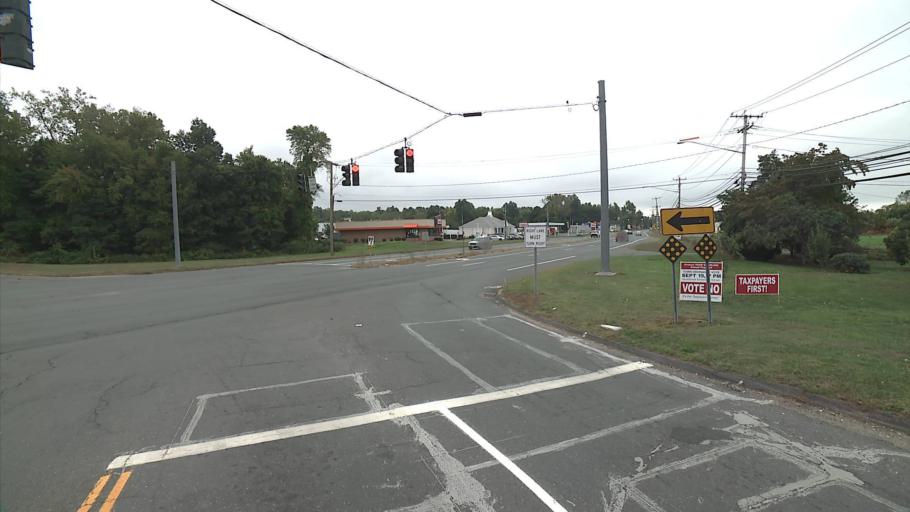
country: US
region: Connecticut
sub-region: Hartford County
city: Windsor Locks
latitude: 41.9137
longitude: -72.6135
